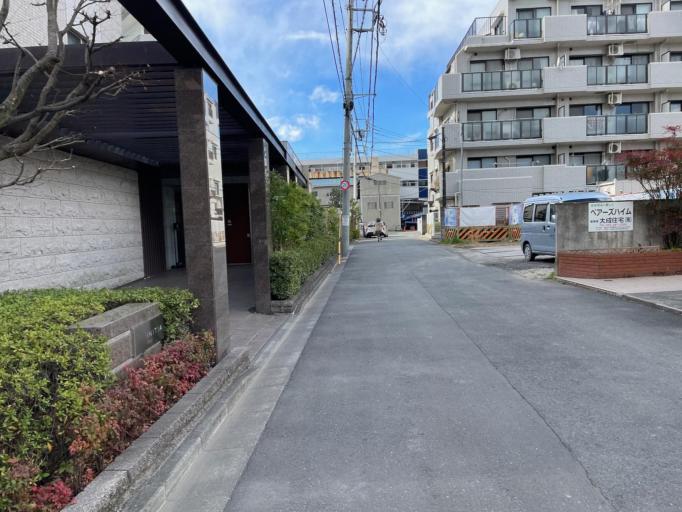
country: JP
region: Tokyo
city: Chofugaoka
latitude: 35.6504
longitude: 139.5320
